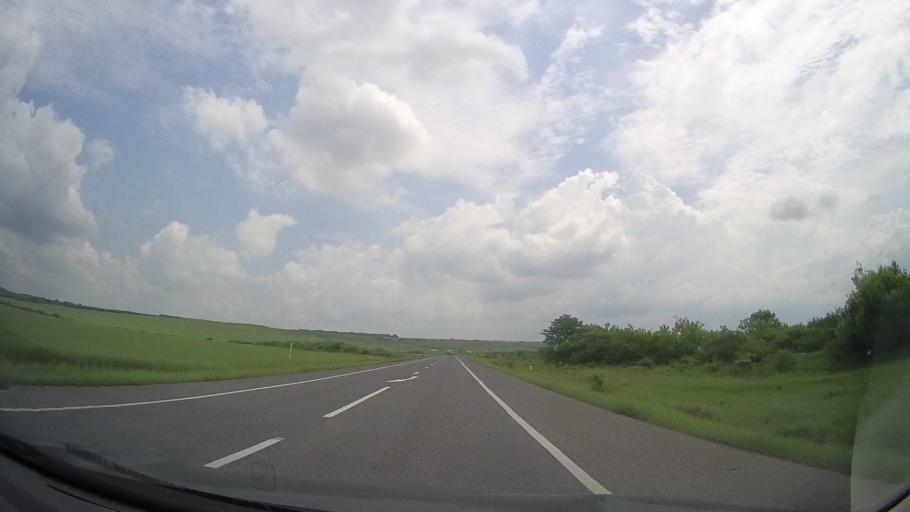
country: RO
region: Timis
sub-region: Municipiul Lugoj
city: Lugoj
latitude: 45.7214
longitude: 21.8829
